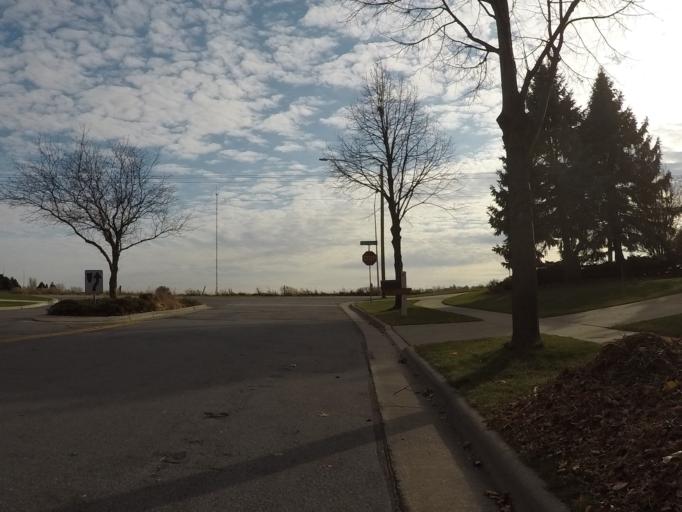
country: US
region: Wisconsin
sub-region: Dane County
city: Middleton
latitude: 43.0753
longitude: -89.5402
